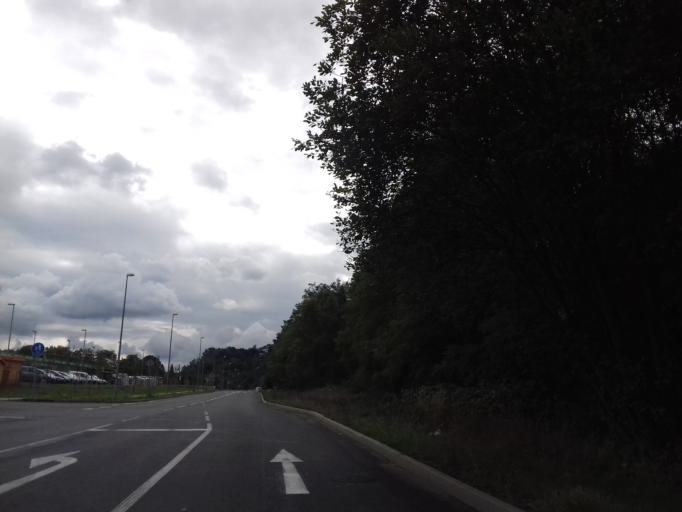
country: CZ
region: Praha
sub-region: Praha 12
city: Modrany
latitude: 50.0185
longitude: 14.3905
